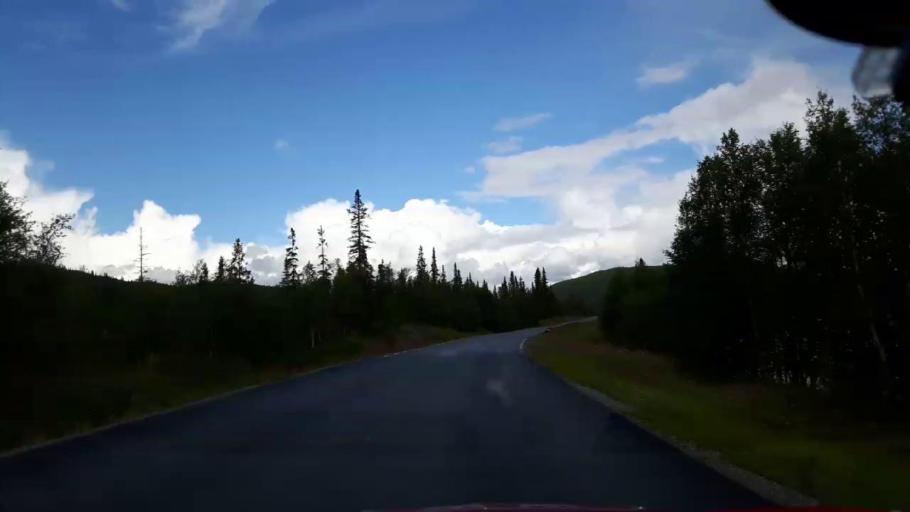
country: SE
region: Vaesterbotten
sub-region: Vilhelmina Kommun
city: Sjoberg
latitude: 65.0117
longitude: 15.1742
